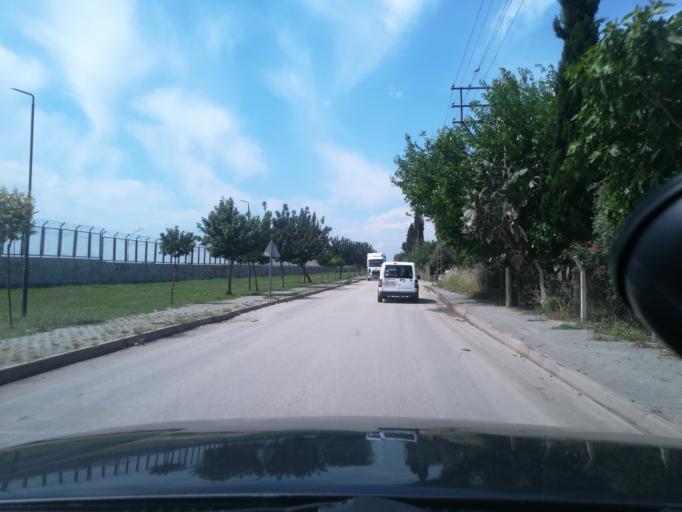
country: TR
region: Adana
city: Seyhan
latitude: 36.9871
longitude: 35.2856
